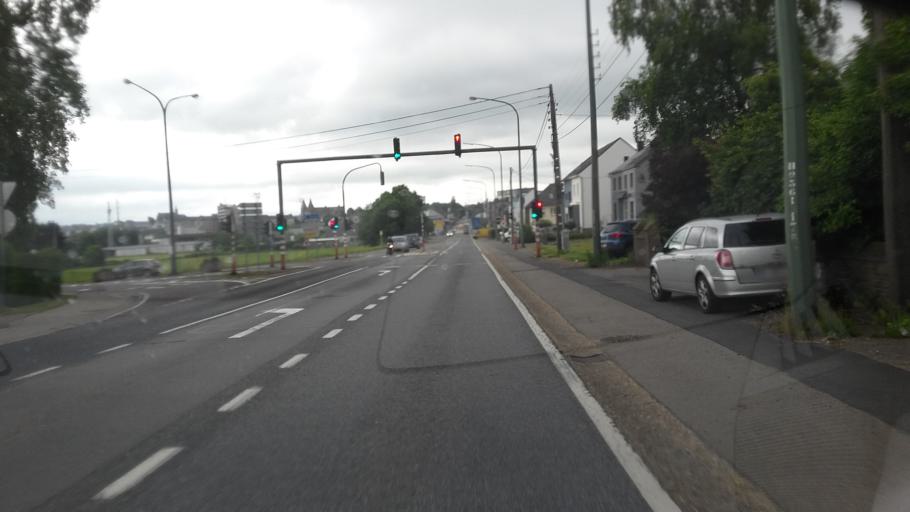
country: BE
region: Wallonia
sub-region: Province du Luxembourg
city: Arlon
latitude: 49.6697
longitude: 5.8242
